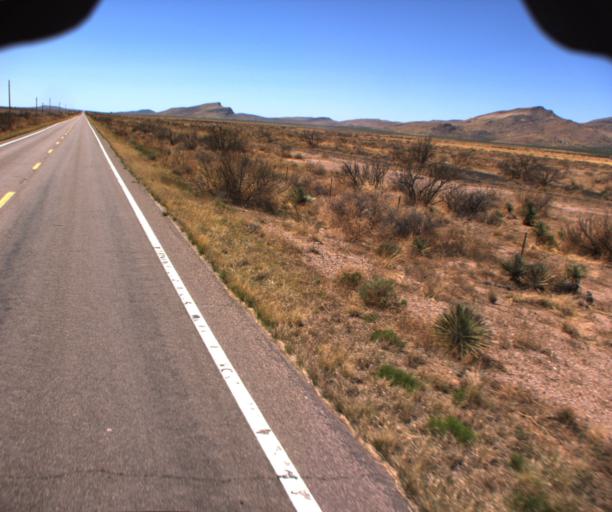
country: US
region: Arizona
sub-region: Cochise County
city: Douglas
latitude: 31.7305
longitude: -109.1051
